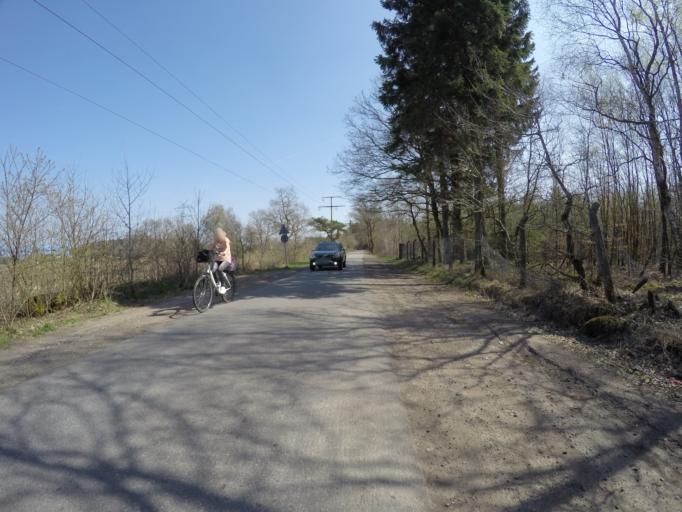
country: DE
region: Schleswig-Holstein
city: Ellerau
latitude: 53.7385
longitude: 9.9301
